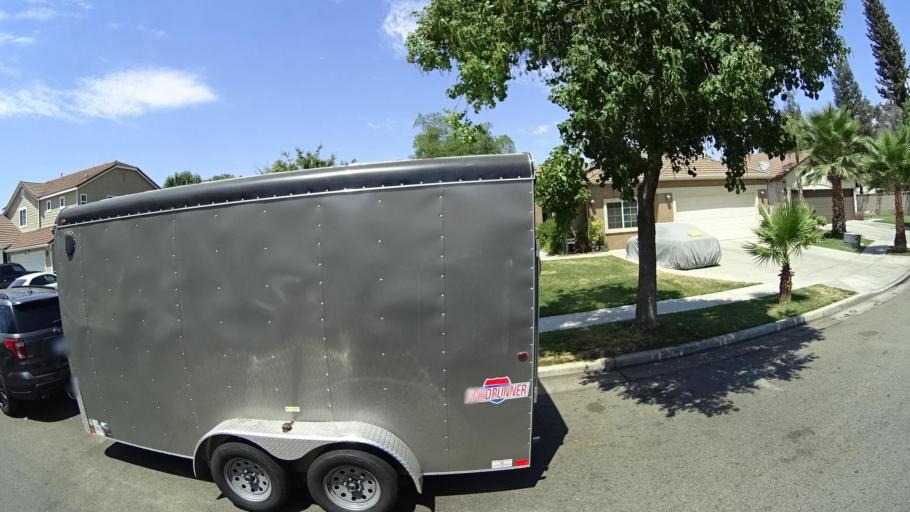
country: US
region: California
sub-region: Fresno County
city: Sunnyside
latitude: 36.7315
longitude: -119.7211
